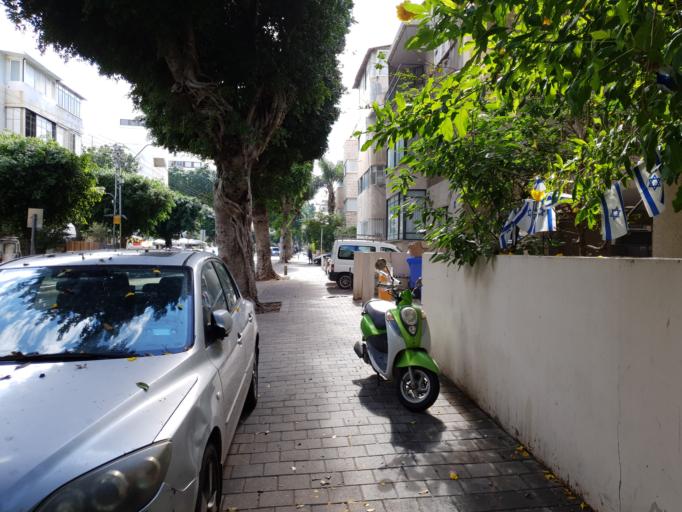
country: IL
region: Tel Aviv
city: Tel Aviv
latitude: 32.0805
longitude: 34.7753
